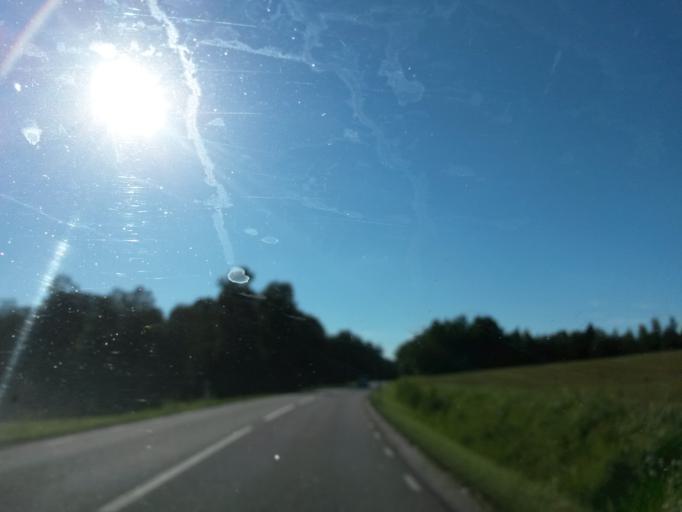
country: SE
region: Vaestra Goetaland
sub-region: Boras Kommun
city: Boras
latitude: 57.8379
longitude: 12.9796
